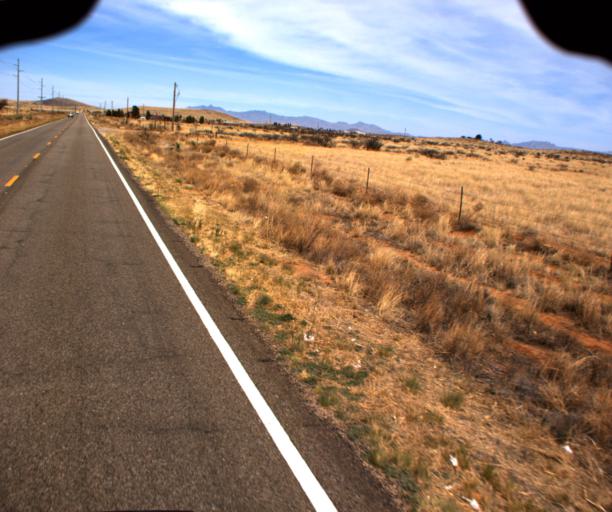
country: US
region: Arizona
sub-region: Cochise County
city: Tombstone
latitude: 31.8682
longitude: -109.6951
